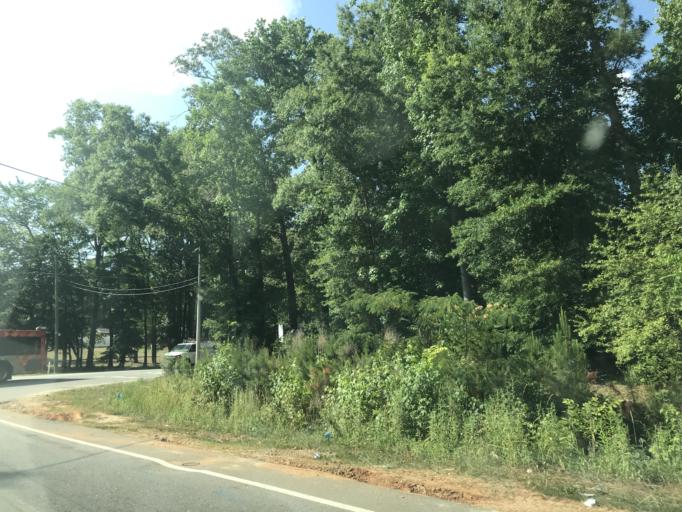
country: US
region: North Carolina
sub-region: Wake County
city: Garner
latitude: 35.7298
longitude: -78.5558
